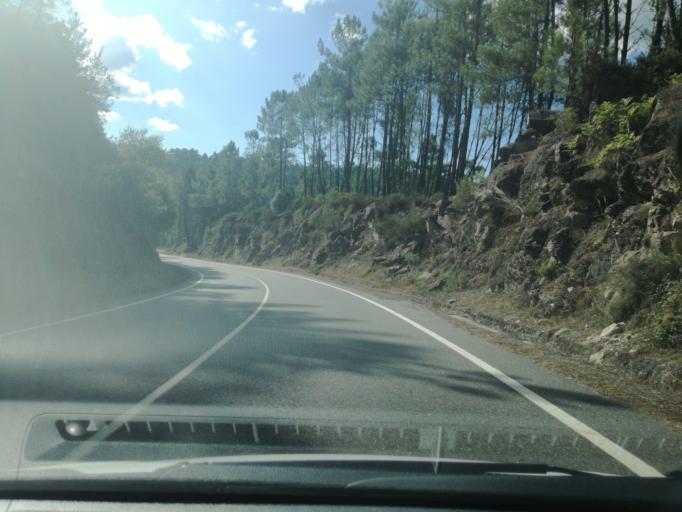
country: ES
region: Galicia
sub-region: Provincia de Ourense
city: Lobios
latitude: 41.9079
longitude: -8.0894
